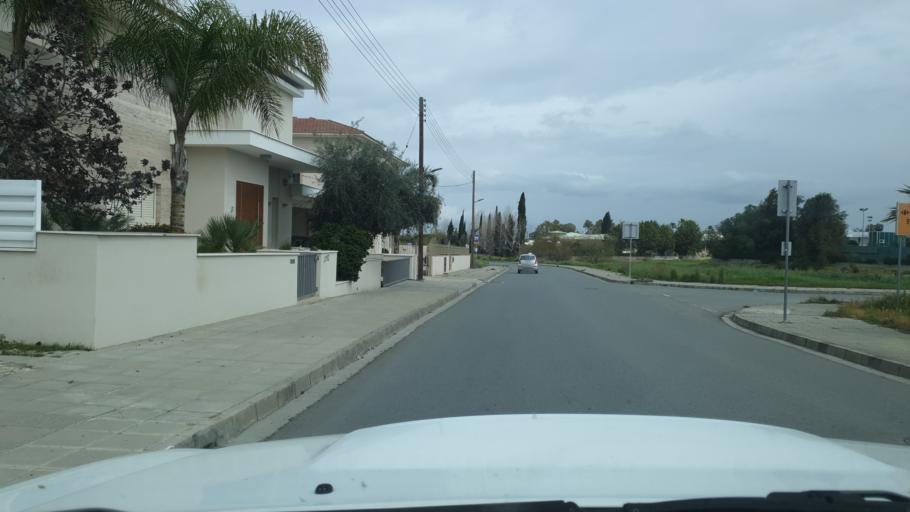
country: CY
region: Lefkosia
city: Tseri
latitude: 35.1033
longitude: 33.3551
